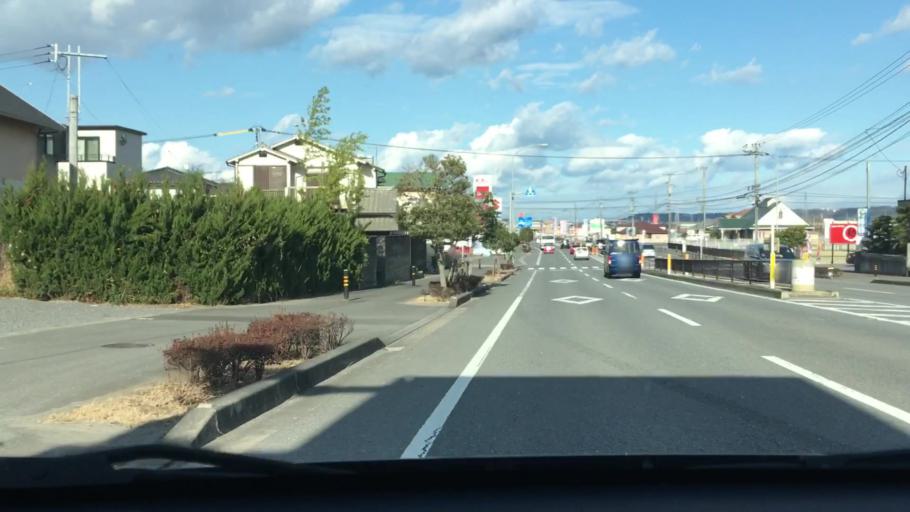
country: JP
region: Oita
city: Tsurusaki
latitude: 33.1877
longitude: 131.6701
